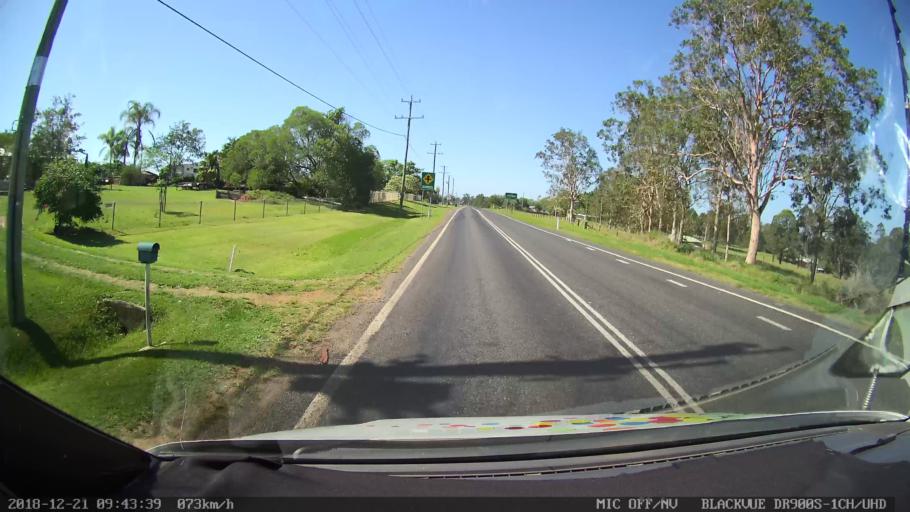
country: AU
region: New South Wales
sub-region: Clarence Valley
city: Grafton
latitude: -29.6092
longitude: 152.9355
